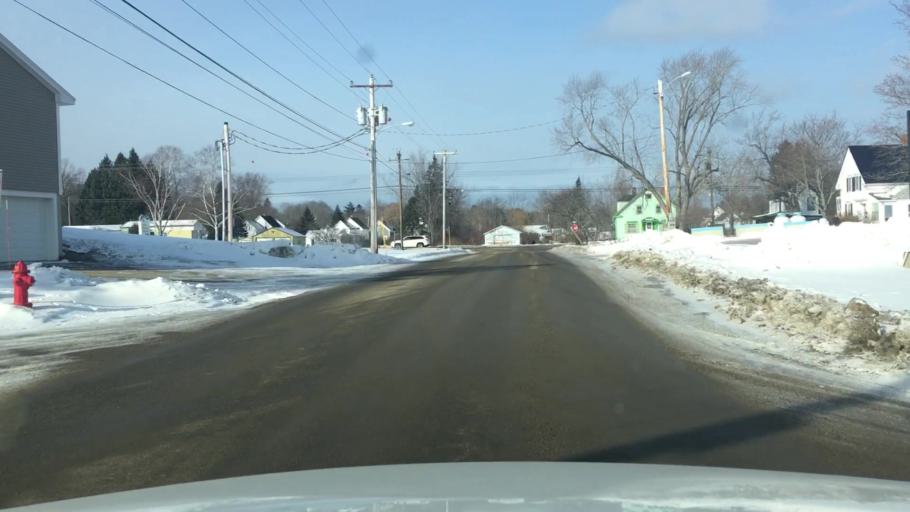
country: US
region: Maine
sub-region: Washington County
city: Calais
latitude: 45.1806
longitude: -67.2692
